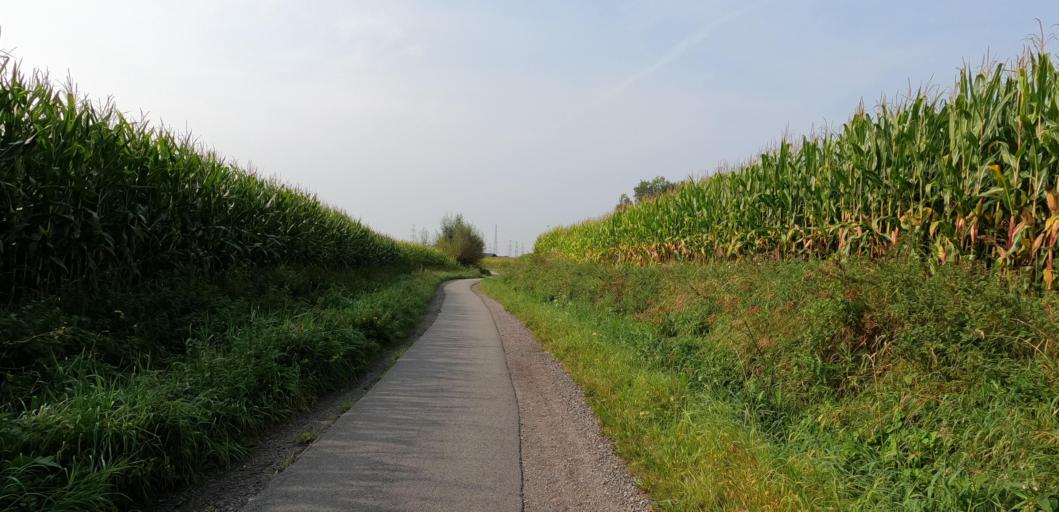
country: BE
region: Flanders
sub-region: Provincie Oost-Vlaanderen
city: Beveren
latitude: 51.1613
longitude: 4.2577
